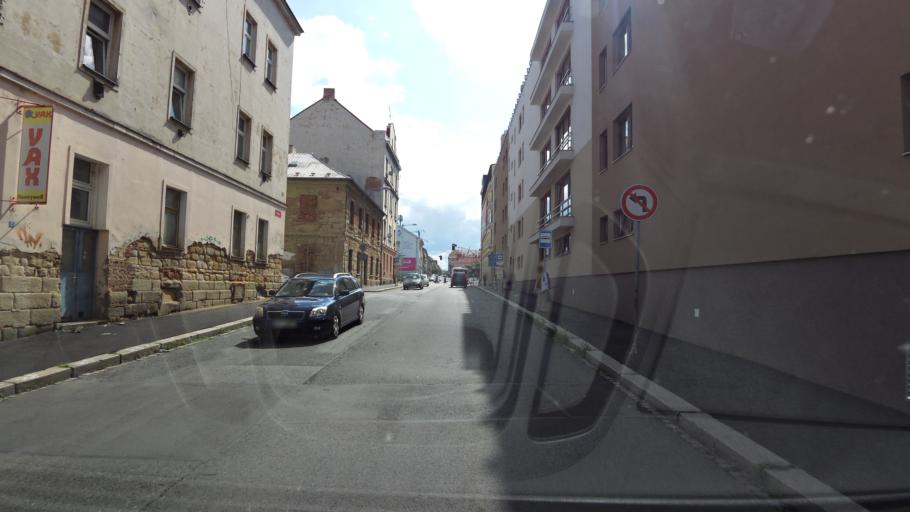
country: CZ
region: Plzensky
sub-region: Okres Plzen-Mesto
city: Pilsen
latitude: 49.7494
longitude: 13.3660
